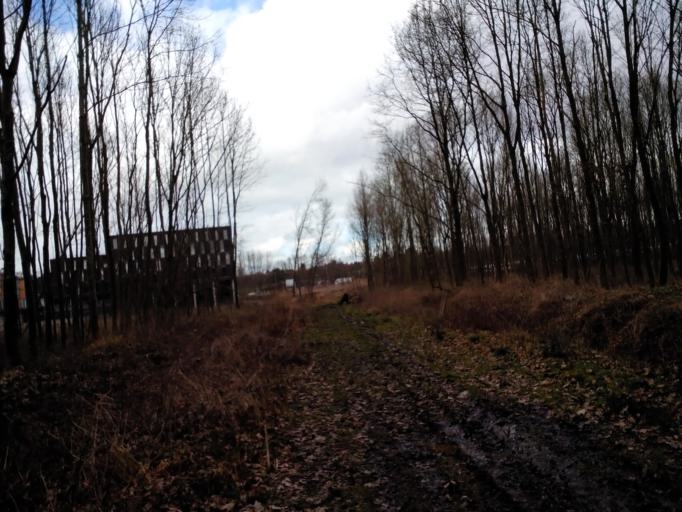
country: BE
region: Flanders
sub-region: Provincie Vlaams-Brabant
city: Oud-Heverlee
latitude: 50.8630
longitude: 4.6703
